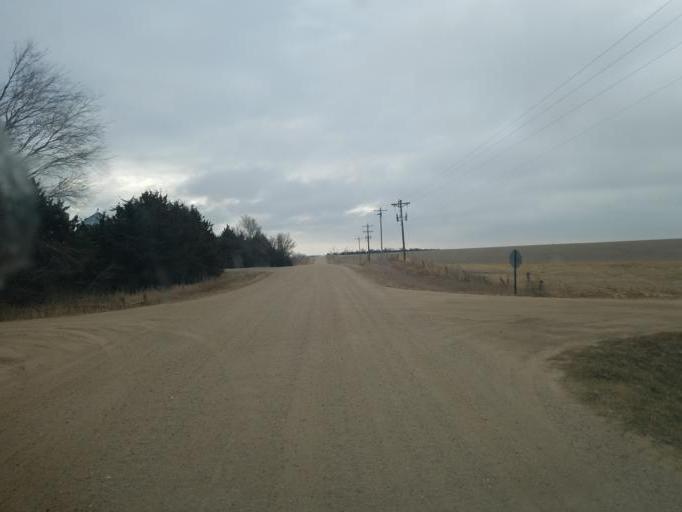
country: US
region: Nebraska
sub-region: Pierce County
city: Plainview
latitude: 42.3942
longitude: -97.7960
